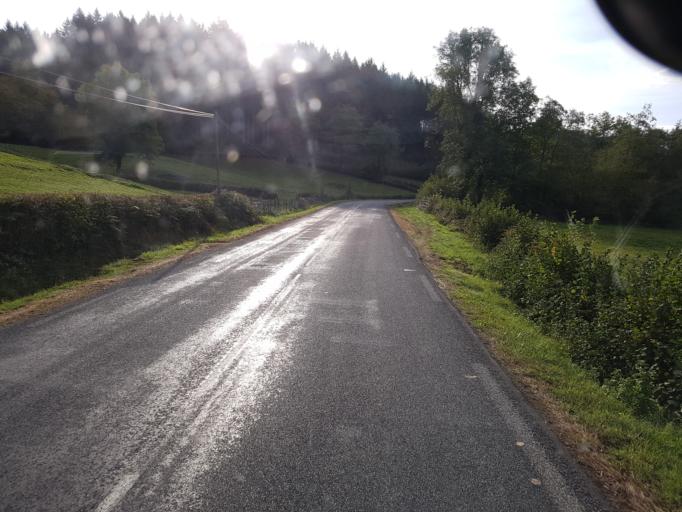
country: FR
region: Bourgogne
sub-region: Departement de Saone-et-Loire
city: Chauffailles
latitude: 46.2263
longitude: 4.4246
